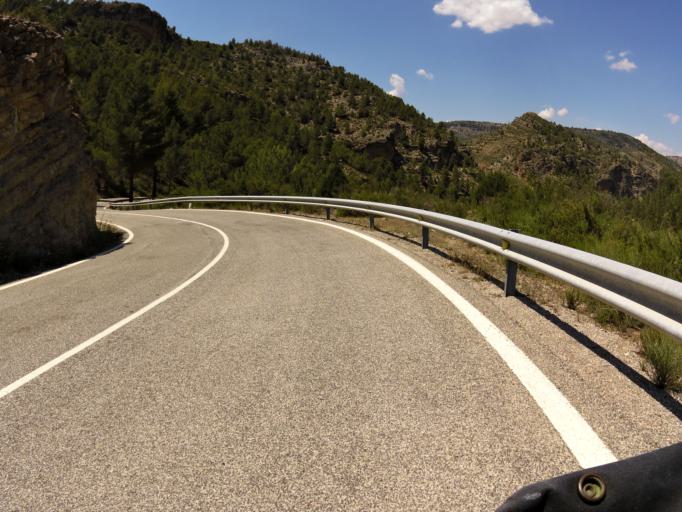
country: ES
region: Valencia
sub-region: Provincia de Valencia
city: Casas Bajas
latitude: 39.9880
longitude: -1.2755
